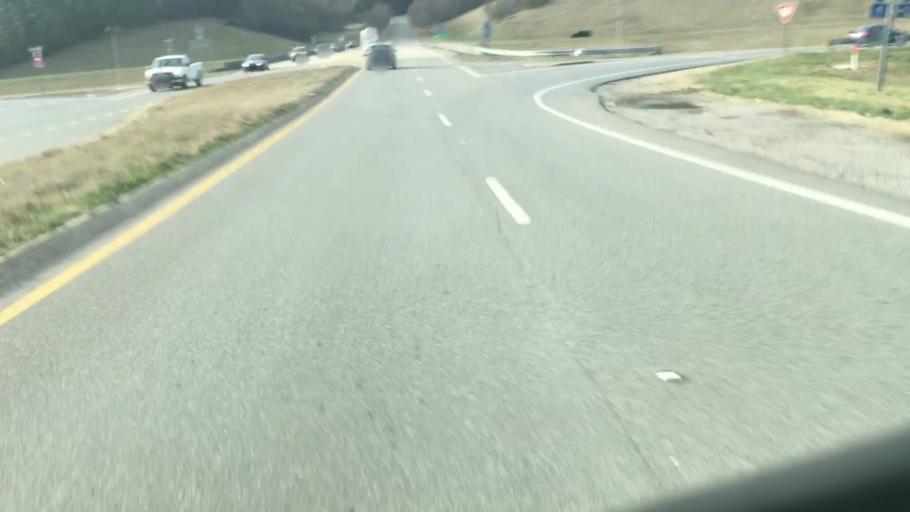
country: US
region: Alabama
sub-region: Jefferson County
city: Cahaba Heights
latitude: 33.4913
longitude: -86.7050
